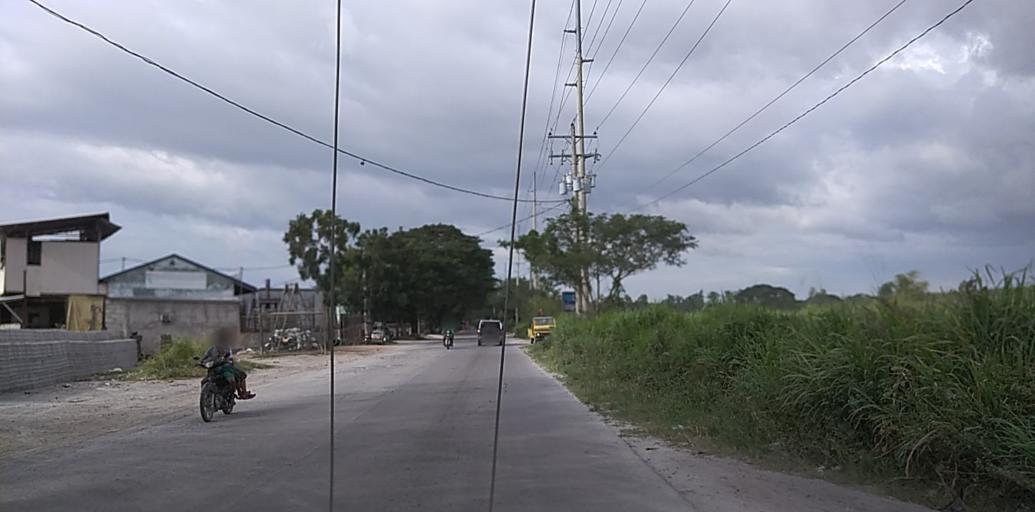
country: PH
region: Central Luzon
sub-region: Province of Pampanga
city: Porac
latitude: 15.0751
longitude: 120.5496
